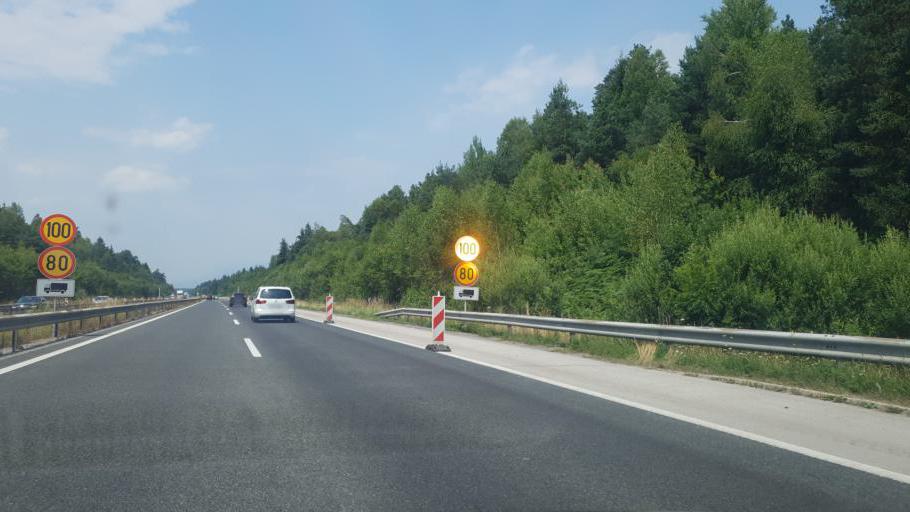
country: SI
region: Vodice
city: Vodice
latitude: 46.2033
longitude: 14.4626
